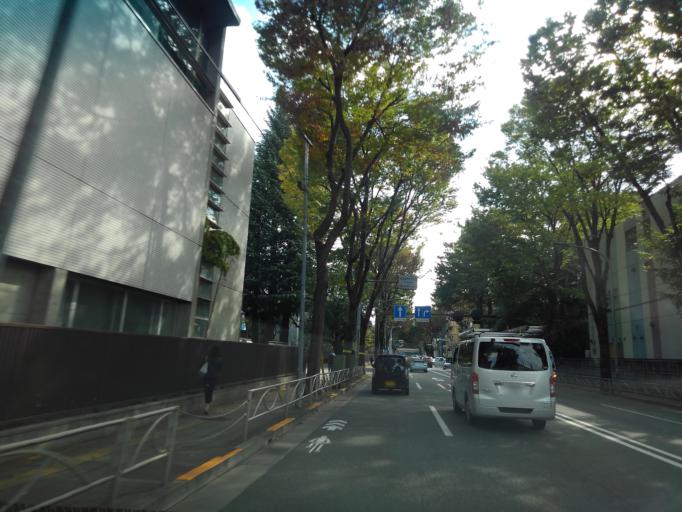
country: JP
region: Tokyo
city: Chofugaoka
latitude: 35.6556
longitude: 139.5433
